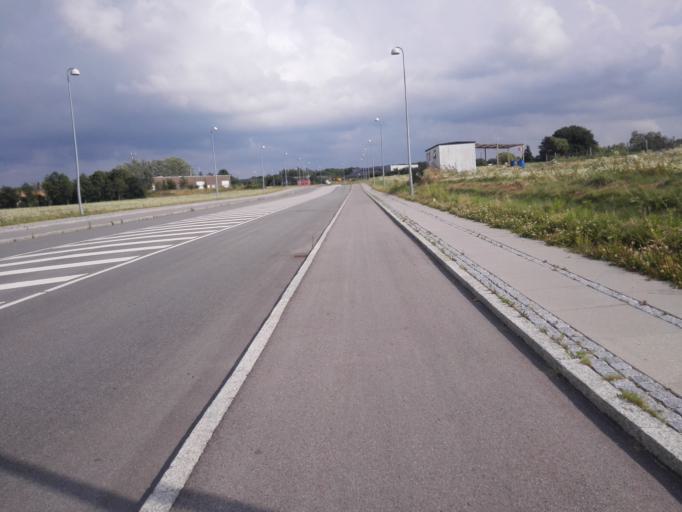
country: DK
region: Capital Region
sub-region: Egedal Kommune
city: Stenlose
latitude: 55.7776
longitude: 12.1902
